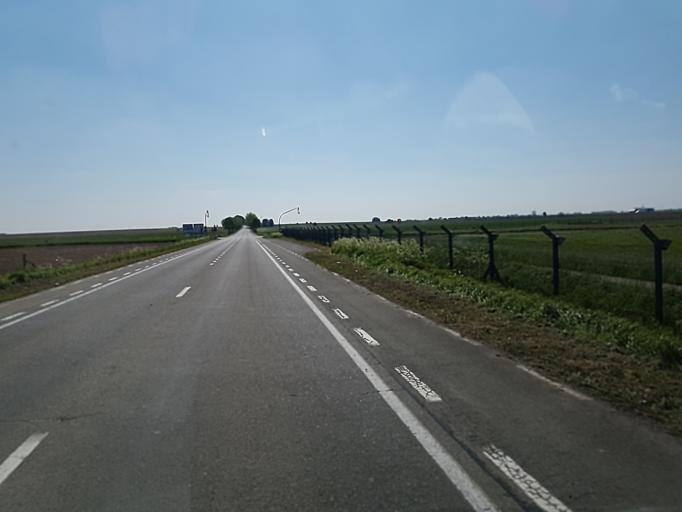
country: BE
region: Wallonia
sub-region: Province du Hainaut
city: Brugelette
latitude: 50.5790
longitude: 3.8606
